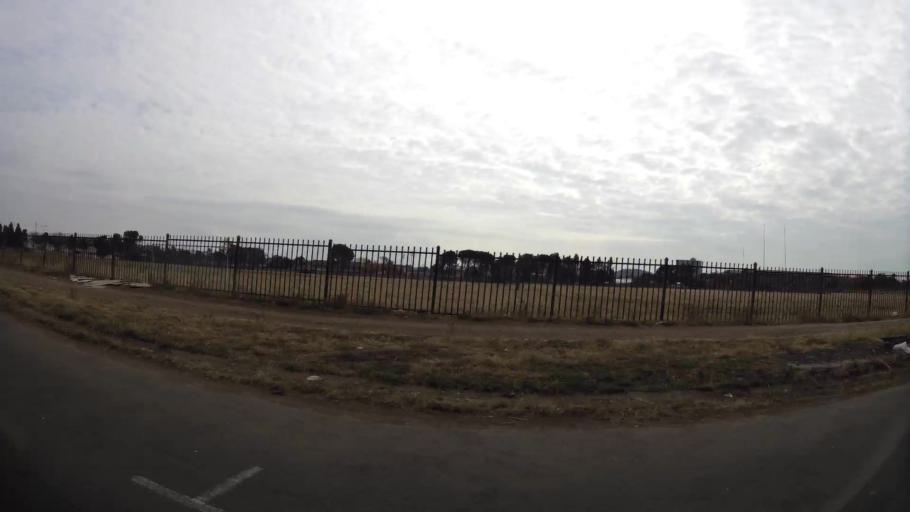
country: ZA
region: Orange Free State
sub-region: Mangaung Metropolitan Municipality
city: Bloemfontein
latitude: -29.1261
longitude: 26.2040
